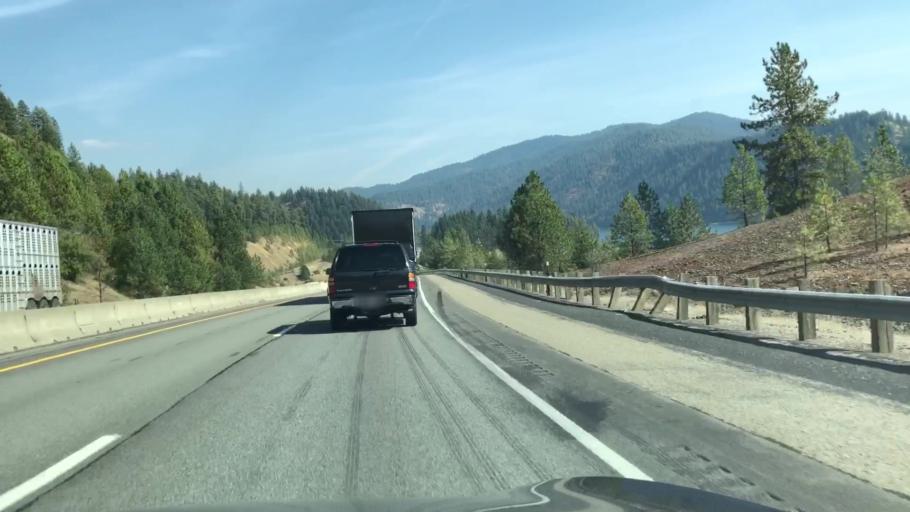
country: US
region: Idaho
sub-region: Kootenai County
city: Coeur d'Alene
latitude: 47.6312
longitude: -116.6920
